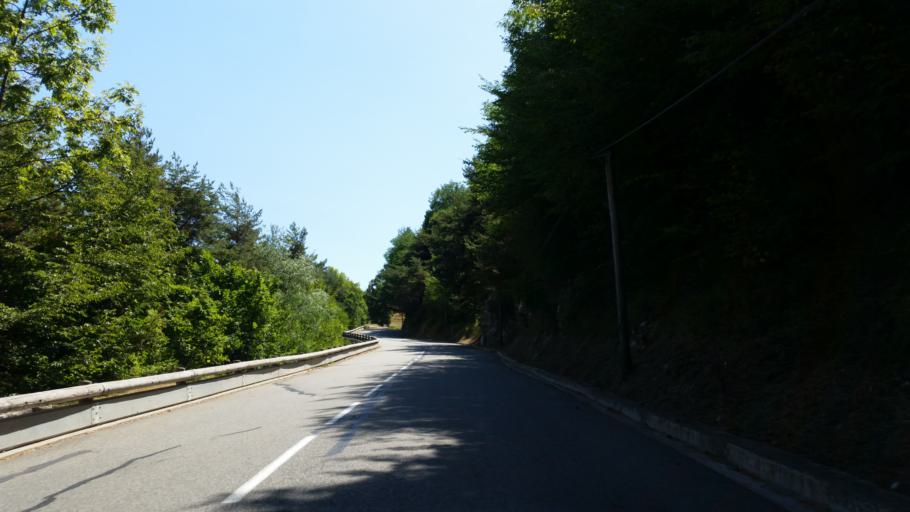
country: FR
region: Provence-Alpes-Cote d'Azur
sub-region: Departement des Alpes-Maritimes
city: Breil-sur-Roya
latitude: 43.9254
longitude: 7.4741
